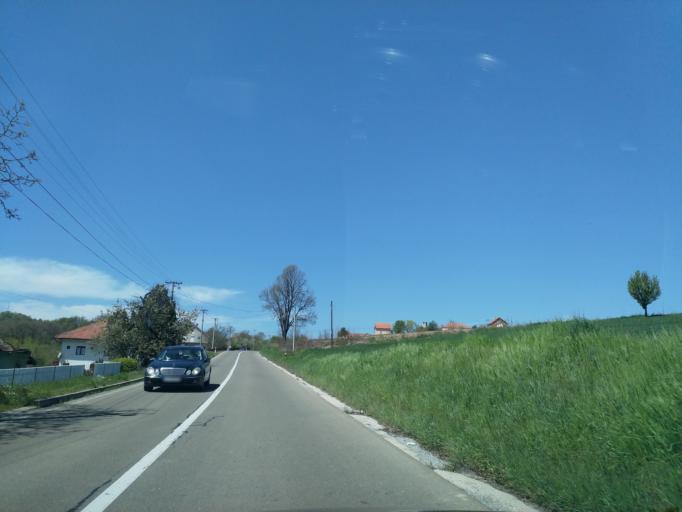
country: RS
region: Central Serbia
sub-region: Belgrade
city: Lazarevac
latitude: 44.3648
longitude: 20.3480
